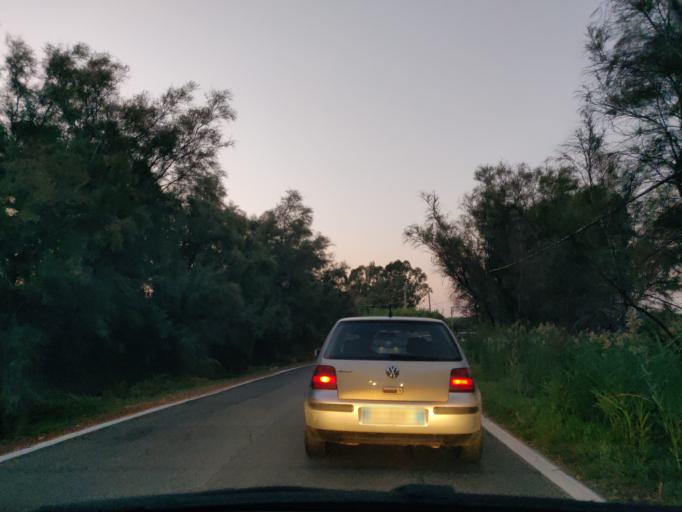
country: IT
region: Latium
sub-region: Citta metropolitana di Roma Capitale
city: Npp 23 (Parco Leonardo)
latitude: 41.8256
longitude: 12.2892
